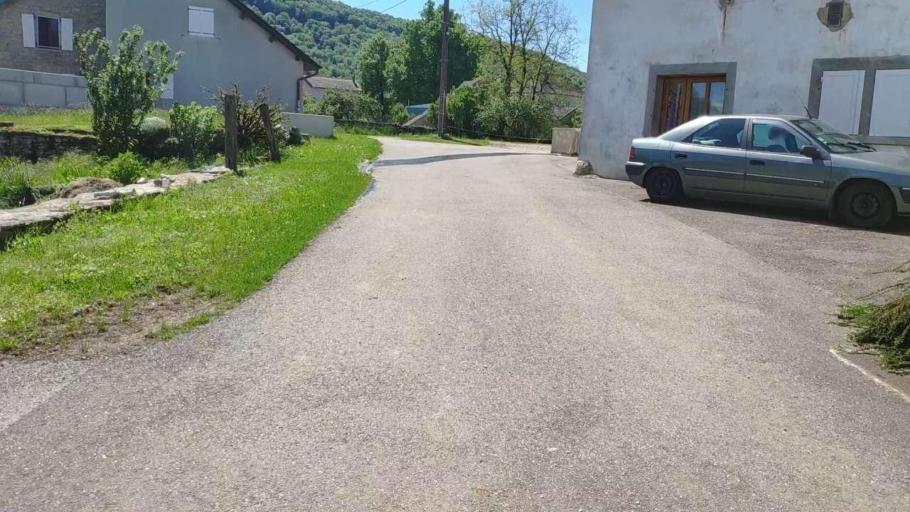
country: FR
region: Franche-Comte
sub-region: Departement du Jura
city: Poligny
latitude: 46.7292
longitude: 5.7460
